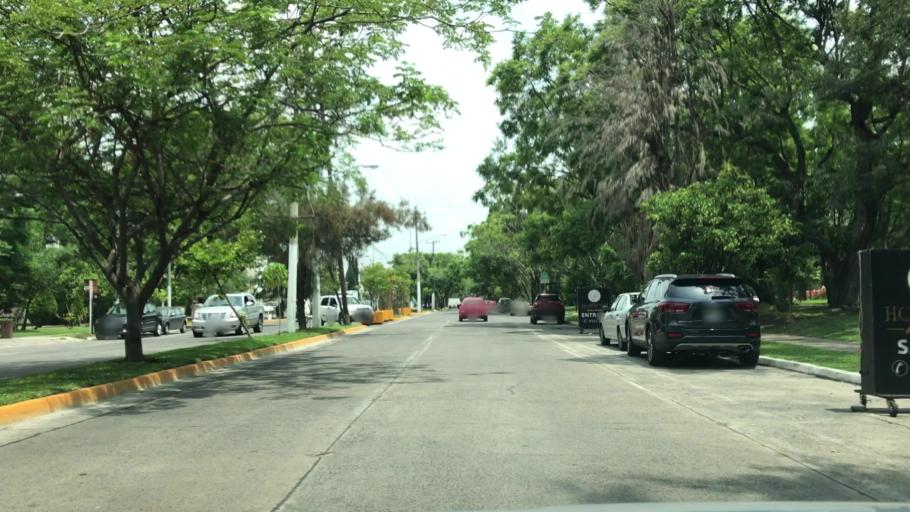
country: MX
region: Jalisco
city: Guadalajara
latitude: 20.6638
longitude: -103.4081
